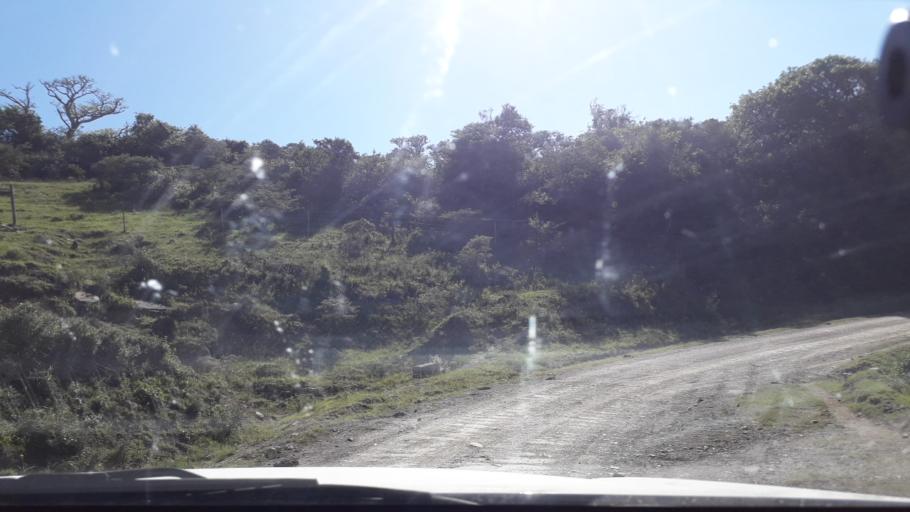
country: ZA
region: Eastern Cape
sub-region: Amathole District Municipality
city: Komga
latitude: -32.7883
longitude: 27.9522
